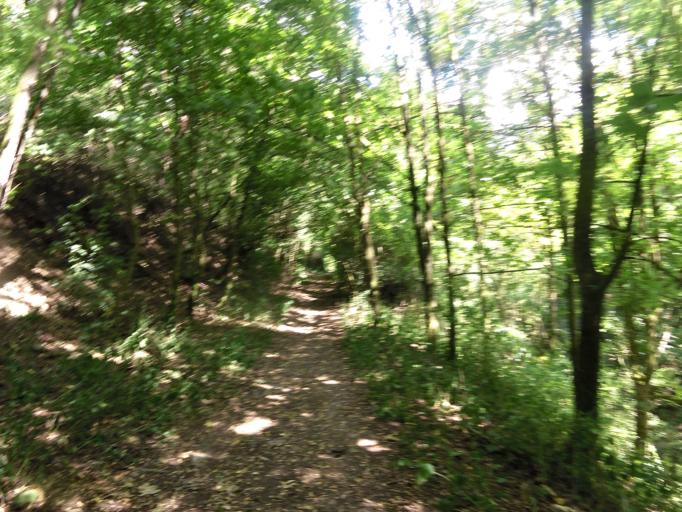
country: DE
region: Bavaria
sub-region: Regierungsbezirk Unterfranken
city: Reichenberg
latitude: 49.7332
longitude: 9.9517
